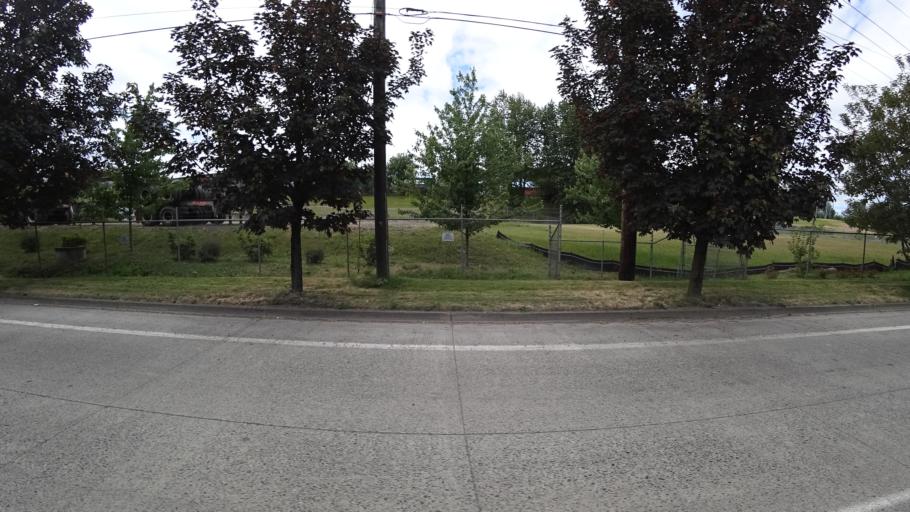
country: US
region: Oregon
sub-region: Washington County
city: West Haven
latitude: 45.6120
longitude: -122.7626
